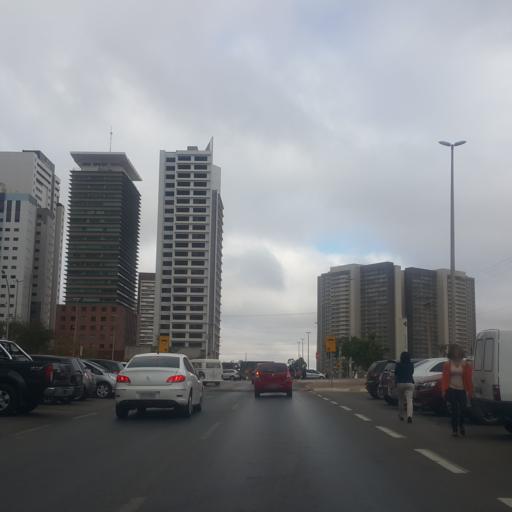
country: BR
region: Federal District
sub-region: Brasilia
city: Brasilia
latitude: -15.8361
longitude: -48.0381
